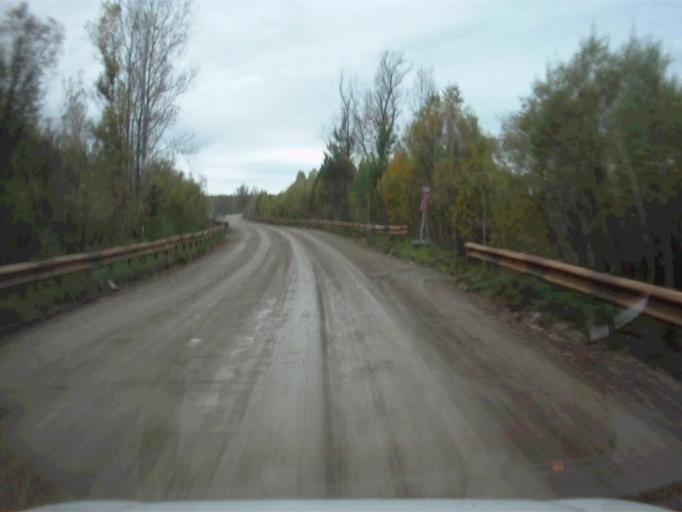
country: RU
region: Chelyabinsk
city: Nyazepetrovsk
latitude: 56.1306
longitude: 59.3258
